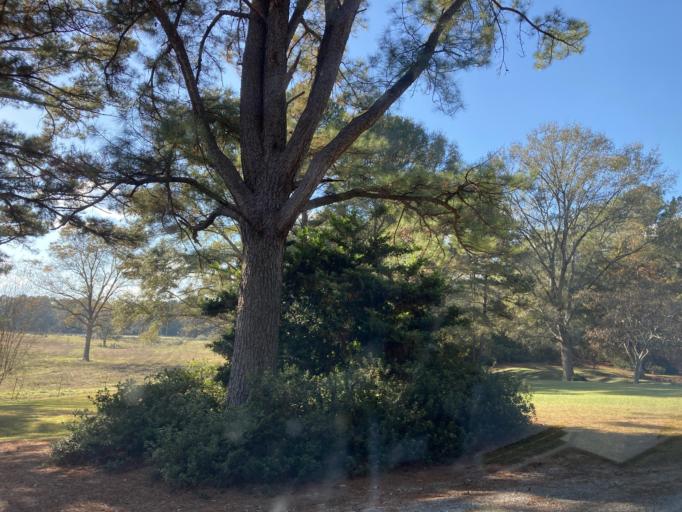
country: US
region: Mississippi
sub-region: Lamar County
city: Sumrall
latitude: 31.4218
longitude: -89.6372
